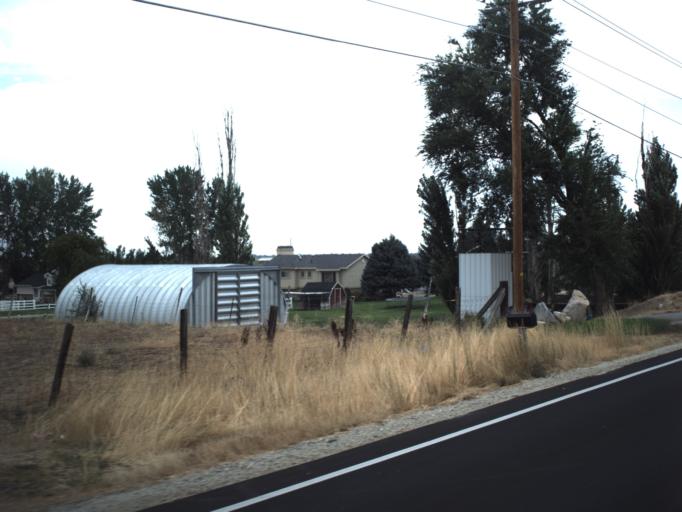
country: US
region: Utah
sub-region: Weber County
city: West Haven
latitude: 41.2098
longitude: -112.0929
